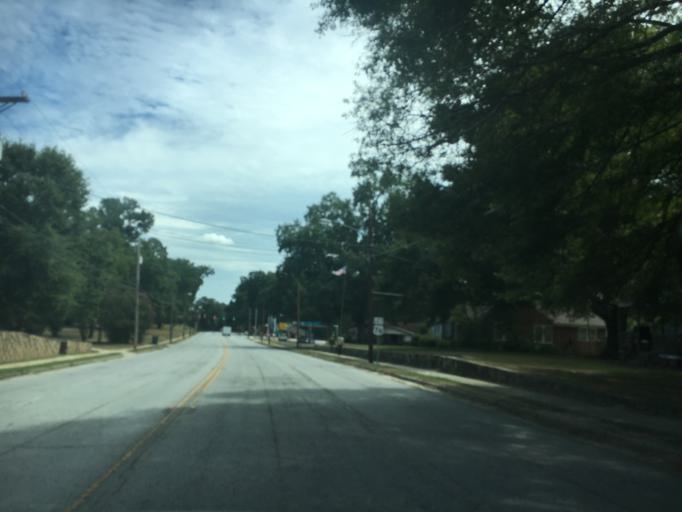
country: US
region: South Carolina
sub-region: Laurens County
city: Laurens
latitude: 34.5083
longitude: -82.0282
